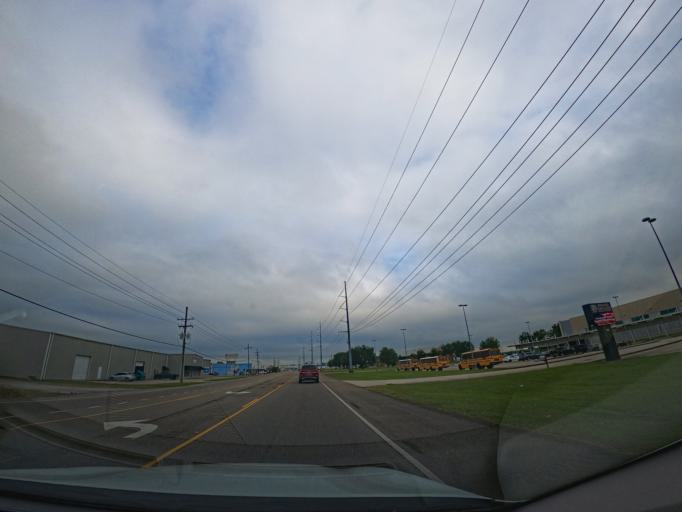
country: US
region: Louisiana
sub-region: Terrebonne Parish
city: Presquille
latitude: 29.5516
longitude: -90.6795
